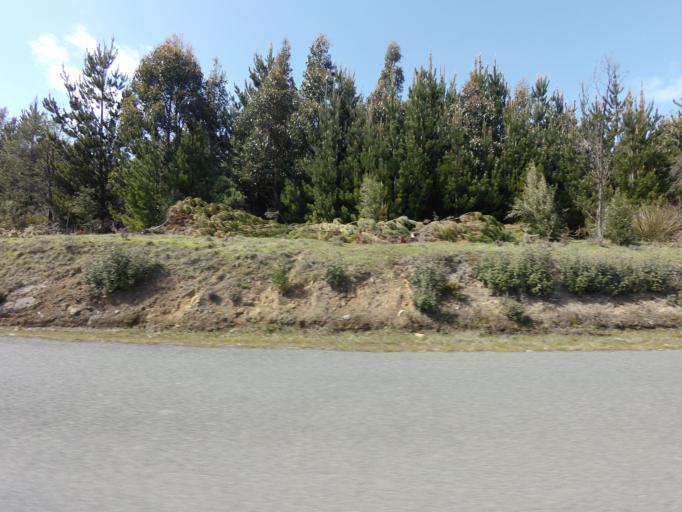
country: AU
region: Tasmania
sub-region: Derwent Valley
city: New Norfolk
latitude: -42.7429
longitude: 146.6568
